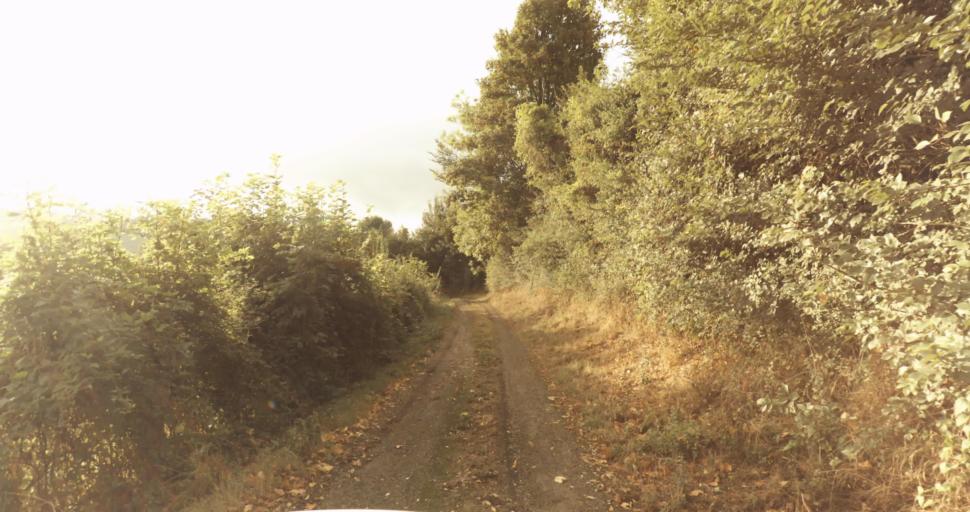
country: FR
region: Lower Normandy
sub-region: Departement de l'Orne
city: Trun
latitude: 48.9145
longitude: 0.0985
